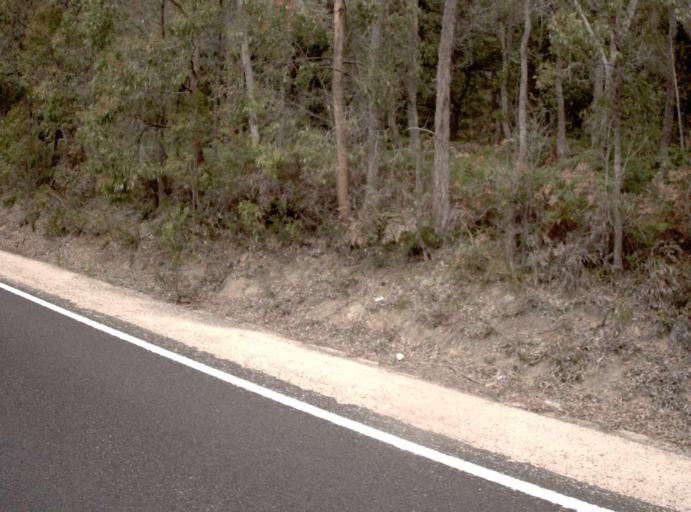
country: AU
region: New South Wales
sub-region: Bega Valley
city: Eden
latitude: -37.4054
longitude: 149.6641
